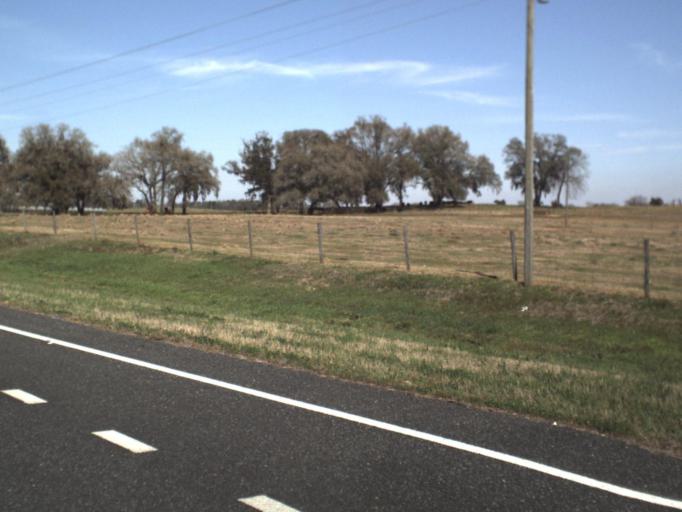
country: US
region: Florida
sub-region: Jackson County
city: Graceville
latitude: 30.8902
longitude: -85.3688
